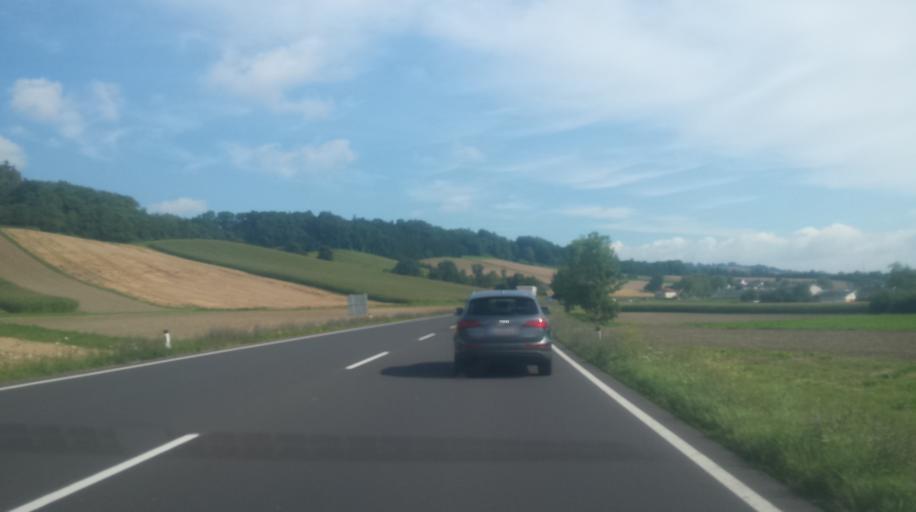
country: AT
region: Upper Austria
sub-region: Politischer Bezirk Grieskirchen
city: Bad Schallerbach
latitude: 48.2113
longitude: 13.9250
